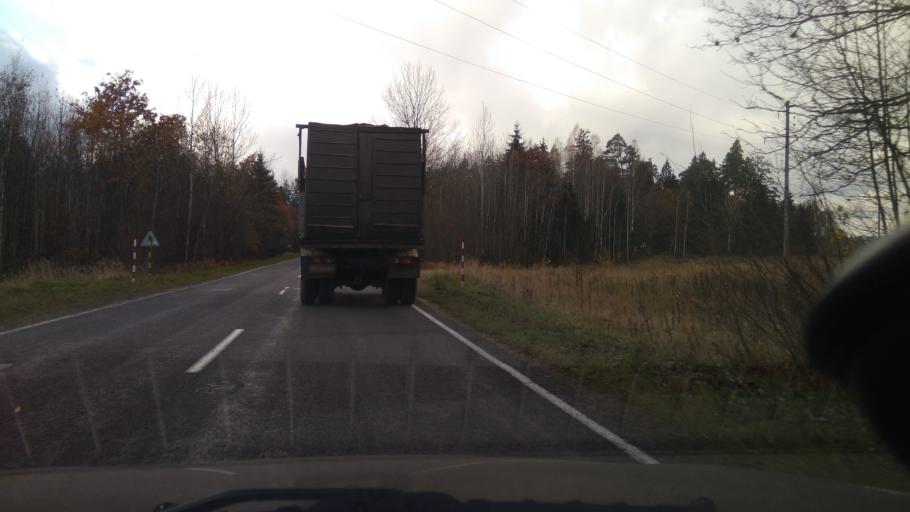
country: BY
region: Minsk
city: Slutsk
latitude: 53.2069
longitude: 27.7743
